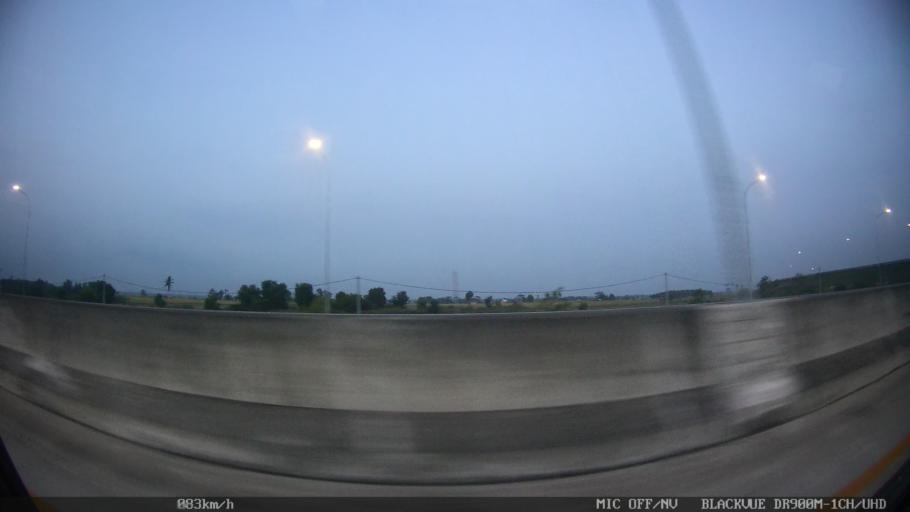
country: ID
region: Lampung
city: Sidorejo
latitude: -5.6070
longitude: 105.5569
